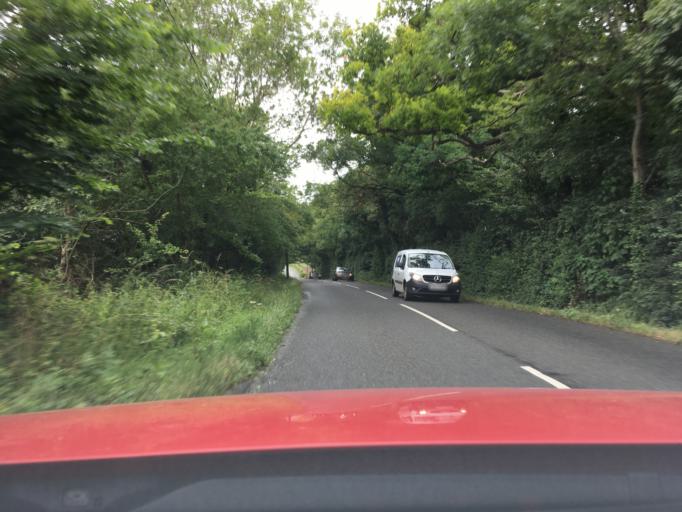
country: GB
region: England
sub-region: Worcestershire
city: Evesham
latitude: 52.0560
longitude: -1.9384
